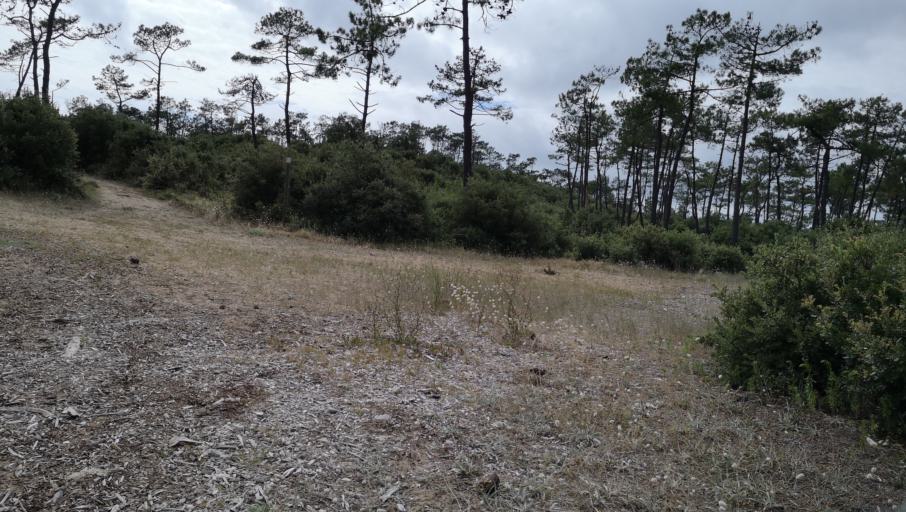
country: FR
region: Pays de la Loire
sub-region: Departement de la Vendee
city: Olonne-sur-Mer
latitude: 46.5348
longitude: -1.8157
